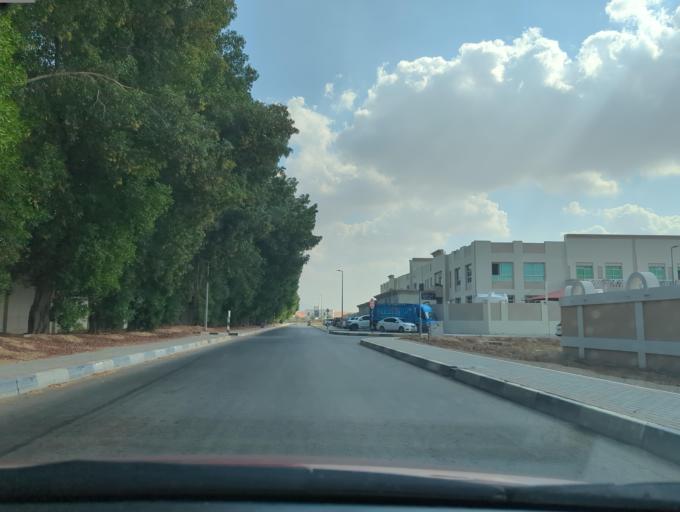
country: AE
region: Abu Dhabi
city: Al Ain
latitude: 24.1554
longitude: 55.6577
